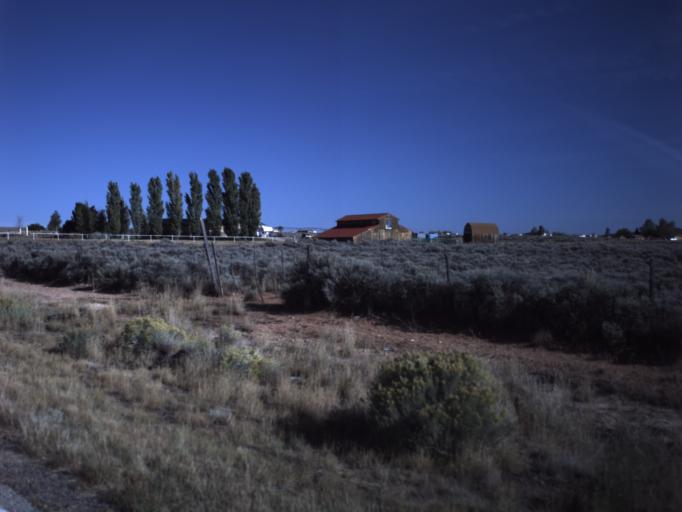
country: US
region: Utah
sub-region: Grand County
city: Moab
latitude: 38.3094
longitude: -109.2886
